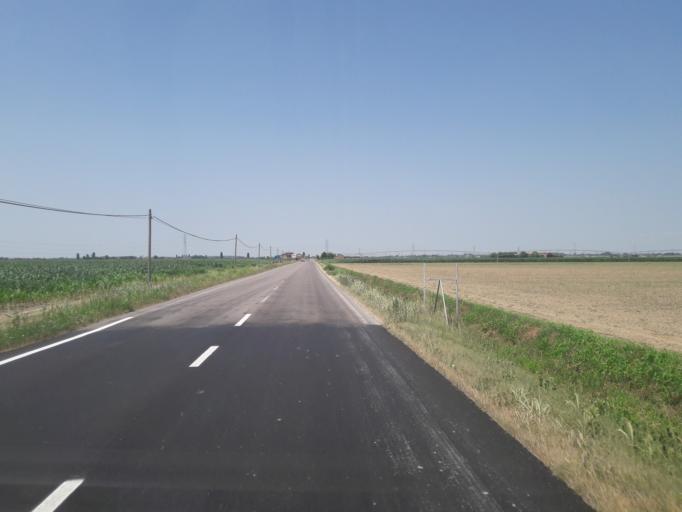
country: IT
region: Veneto
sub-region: Provincia di Rovigo
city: Taglio di Po
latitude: 45.0045
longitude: 12.1918
